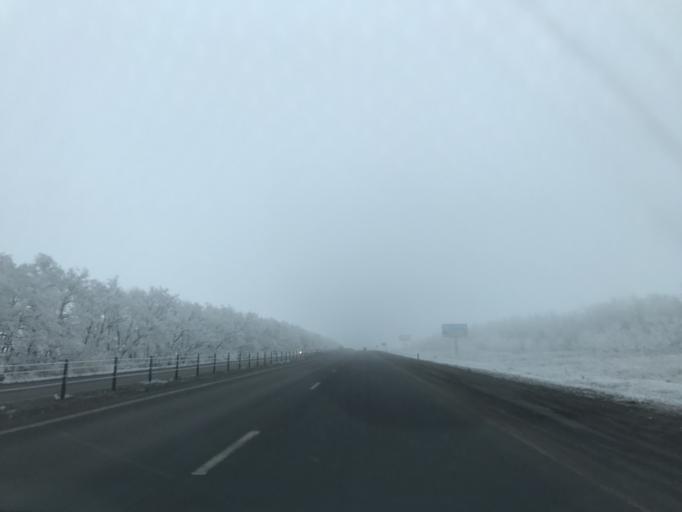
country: RU
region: Rostov
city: Likhoy
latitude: 48.1710
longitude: 40.2638
